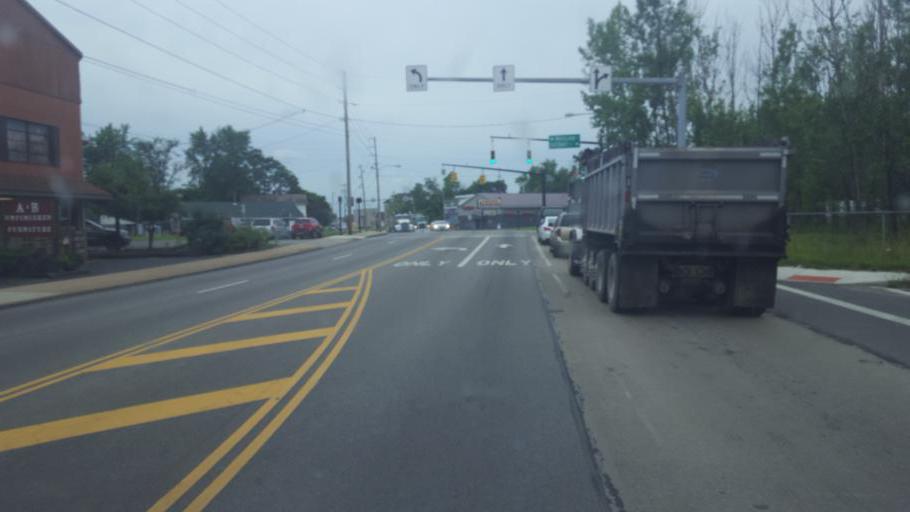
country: US
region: Ohio
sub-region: Trumbull County
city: Warren
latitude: 41.2419
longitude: -80.8092
